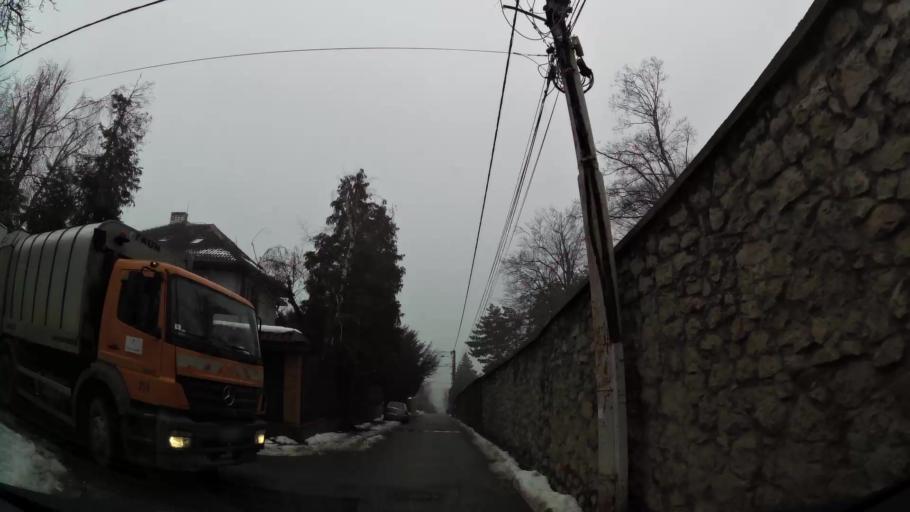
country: RS
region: Central Serbia
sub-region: Belgrade
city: Cukarica
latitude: 44.7872
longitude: 20.4361
